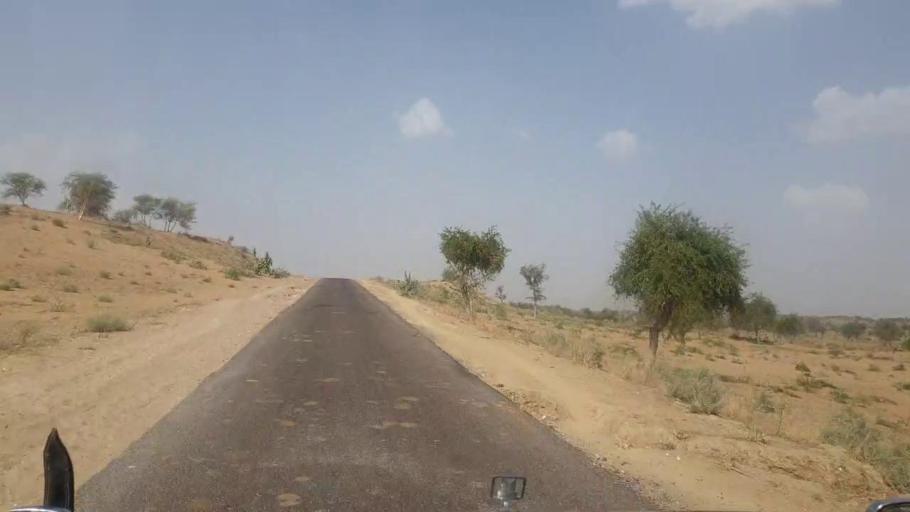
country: PK
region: Sindh
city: Islamkot
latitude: 25.1661
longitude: 70.2878
